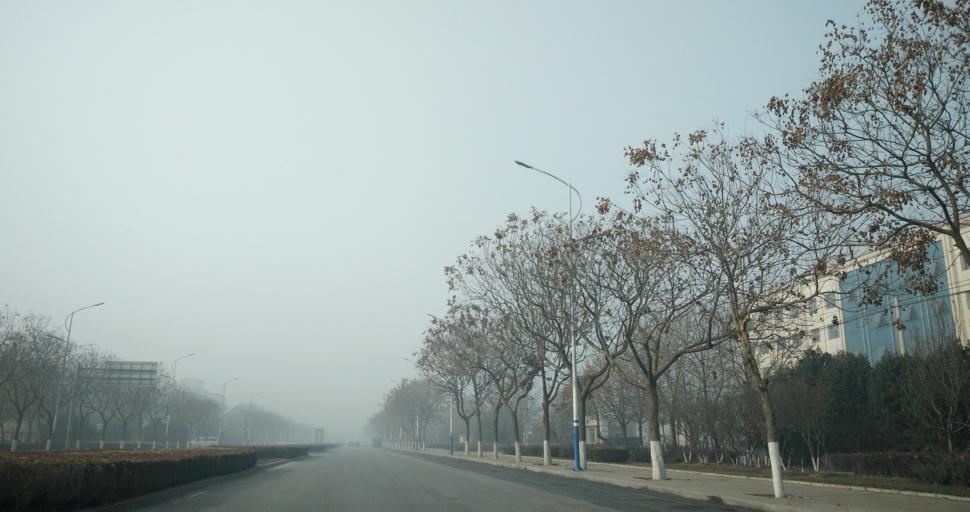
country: CN
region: Beijing
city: Yinghai
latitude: 39.7086
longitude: 116.4145
